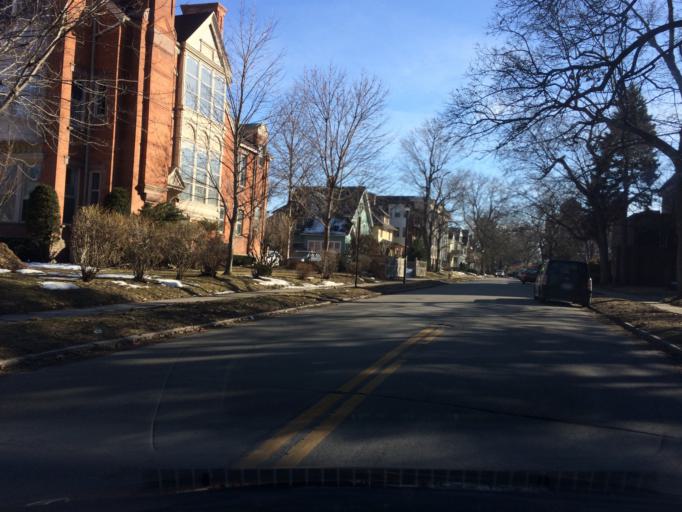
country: US
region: New York
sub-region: Monroe County
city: Rochester
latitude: 43.1526
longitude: -77.5850
